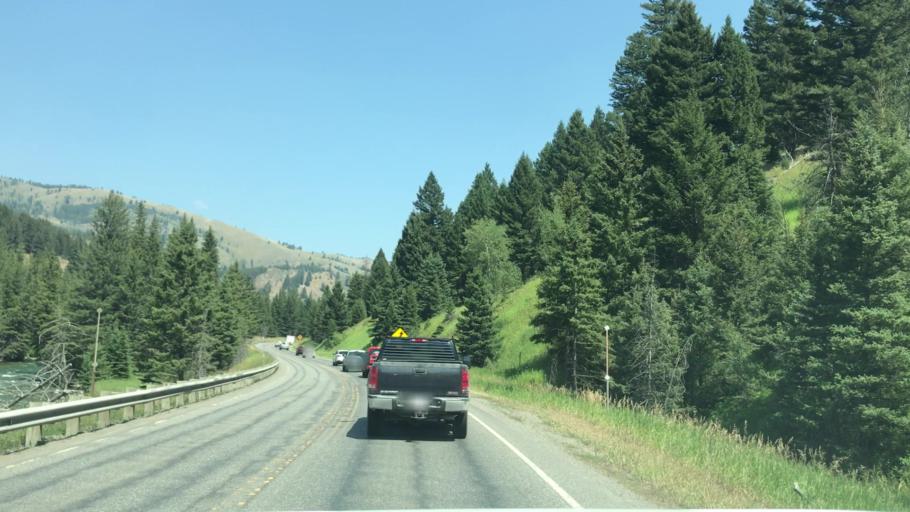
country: US
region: Montana
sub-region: Gallatin County
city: Big Sky
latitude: 45.2847
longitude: -111.2227
